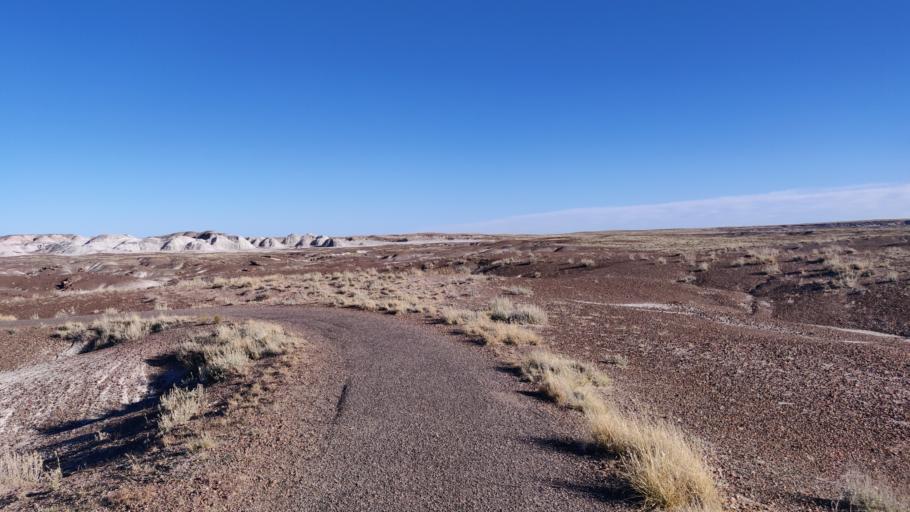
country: US
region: Arizona
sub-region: Navajo County
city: Holbrook
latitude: 34.8644
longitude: -109.7885
